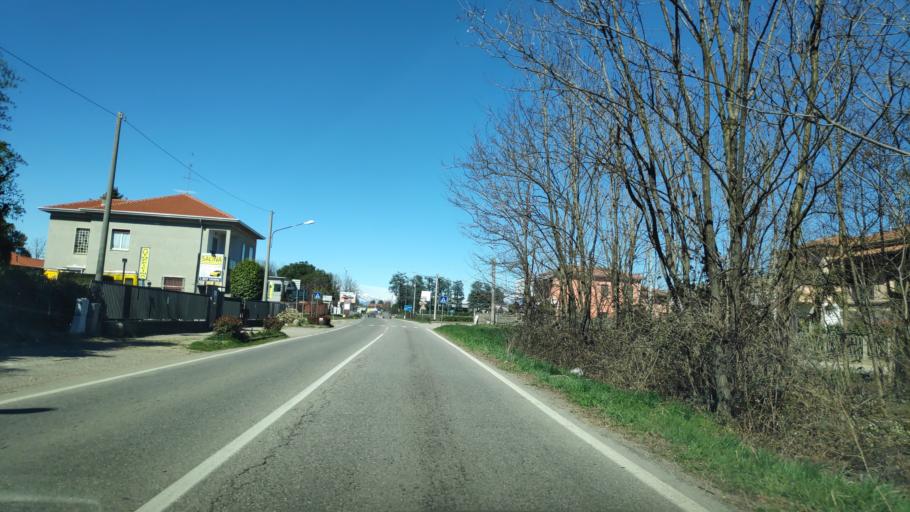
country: IT
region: Lombardy
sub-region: Provincia di Varese
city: Fagnano Olona-Bergoro
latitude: 45.6608
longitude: 8.8428
